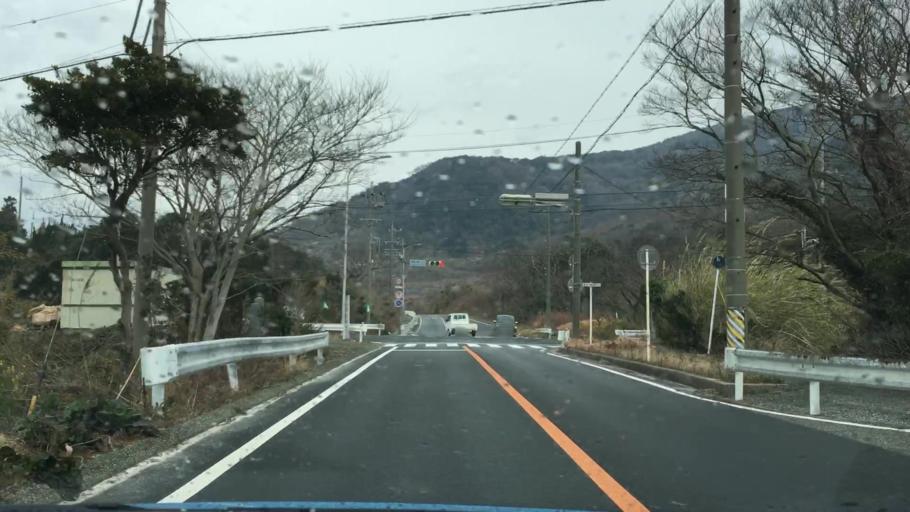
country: JP
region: Aichi
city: Tahara
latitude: 34.6787
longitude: 137.2502
